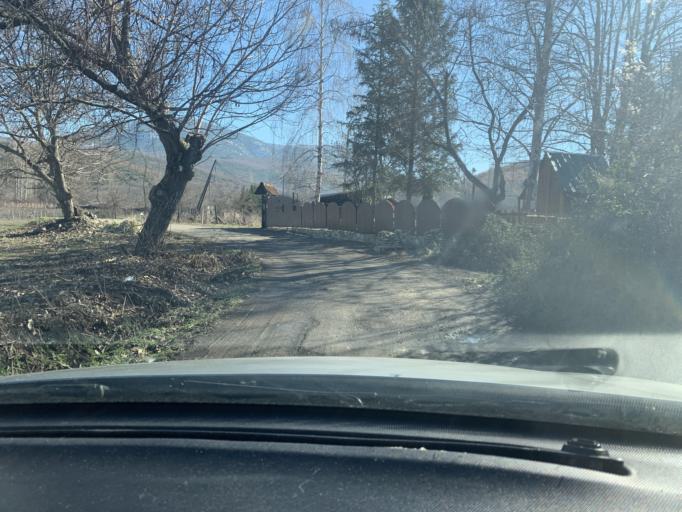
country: MK
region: Demir Kapija
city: Demir Kapija
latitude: 41.3910
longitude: 22.2231
